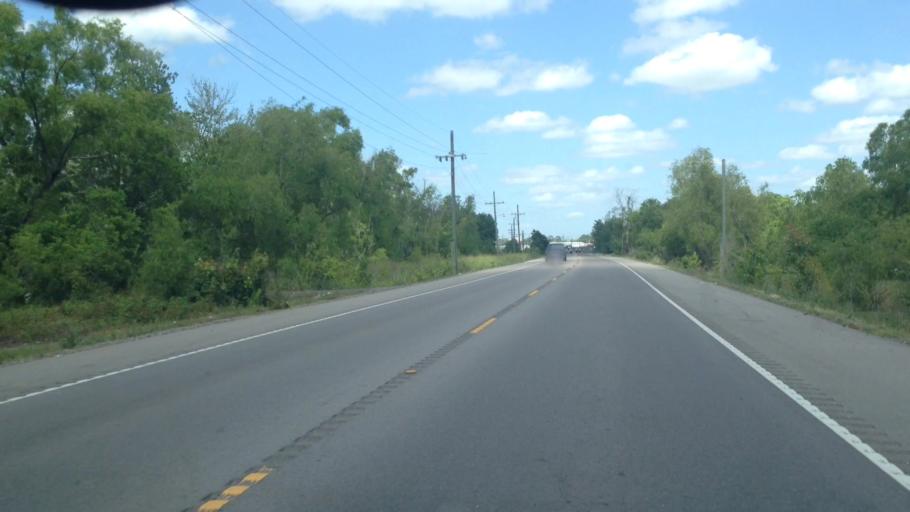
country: US
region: Louisiana
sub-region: Terrebonne Parish
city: Houma
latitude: 29.6392
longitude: -90.6943
